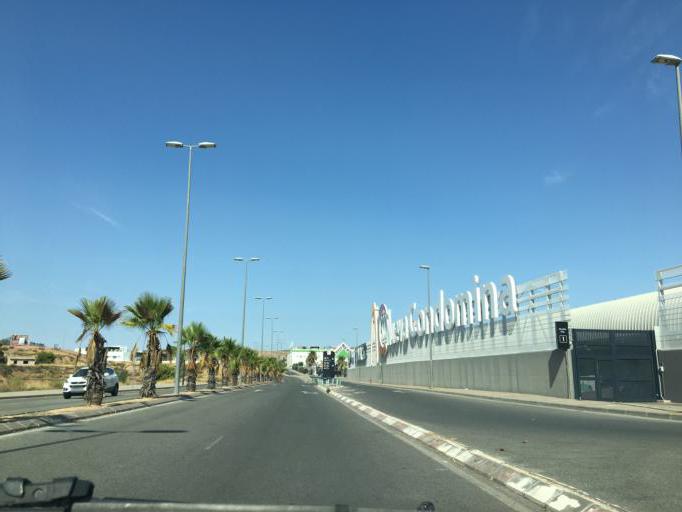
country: ES
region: Murcia
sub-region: Murcia
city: Murcia
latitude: 38.0373
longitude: -1.1476
